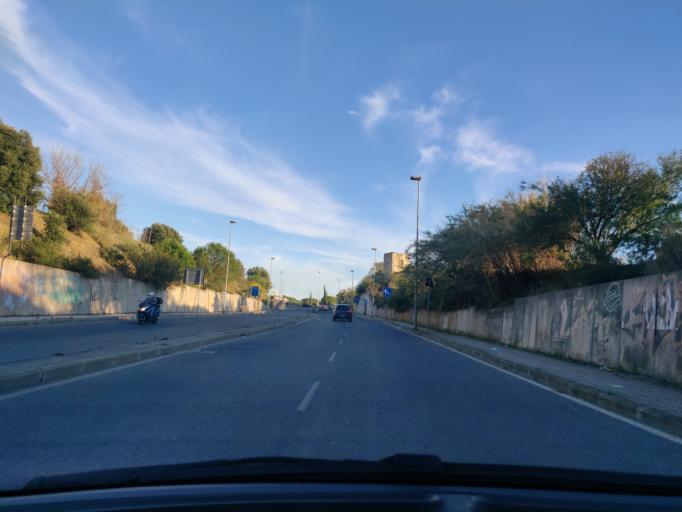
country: IT
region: Latium
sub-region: Citta metropolitana di Roma Capitale
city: Civitavecchia
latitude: 42.1020
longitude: 11.7937
